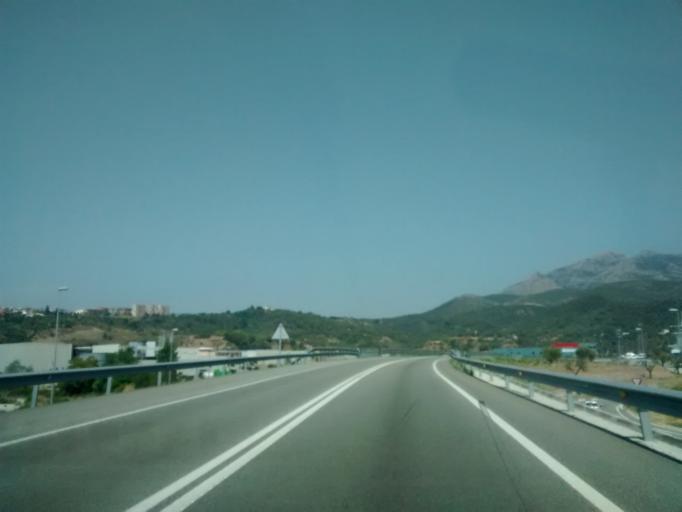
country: ES
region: Catalonia
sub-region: Provincia de Barcelona
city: Olesa de Montserrat
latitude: 41.5436
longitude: 1.8839
